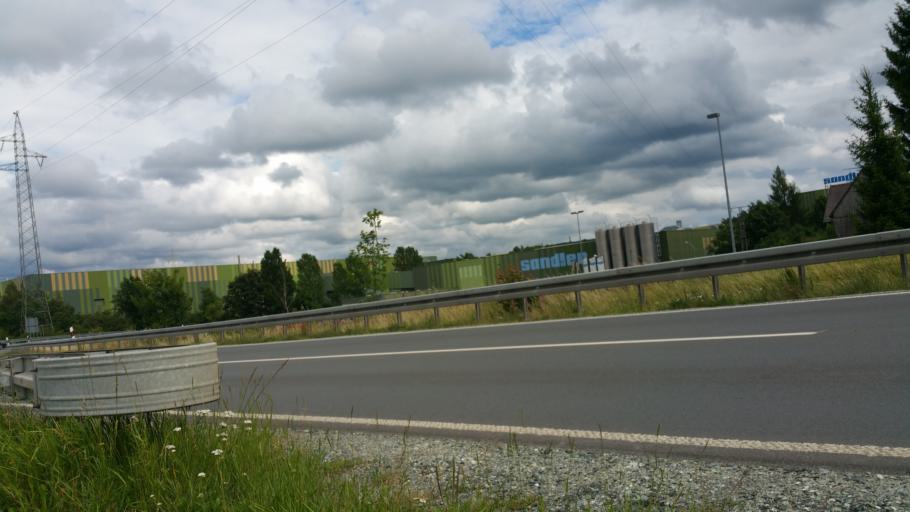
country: DE
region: Bavaria
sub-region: Upper Franconia
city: Schwarzenbach an der Saale
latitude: 50.2266
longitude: 11.9536
